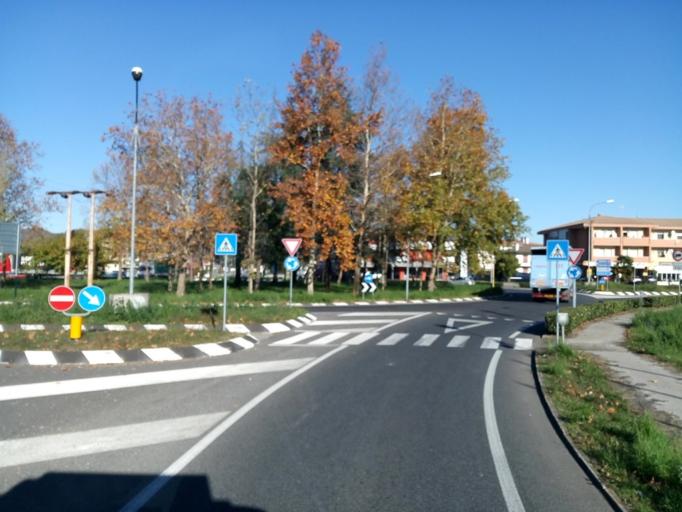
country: IT
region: Veneto
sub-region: Provincia di Treviso
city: Caerano di San Marco
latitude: 45.7857
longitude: 11.9939
